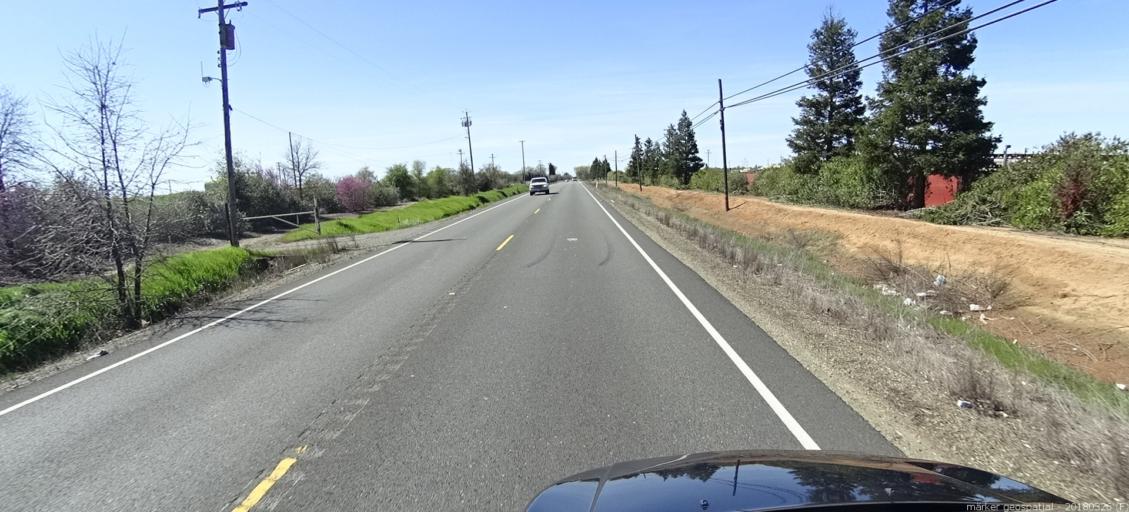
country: US
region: California
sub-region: Sacramento County
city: Rosemont
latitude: 38.5254
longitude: -121.3214
